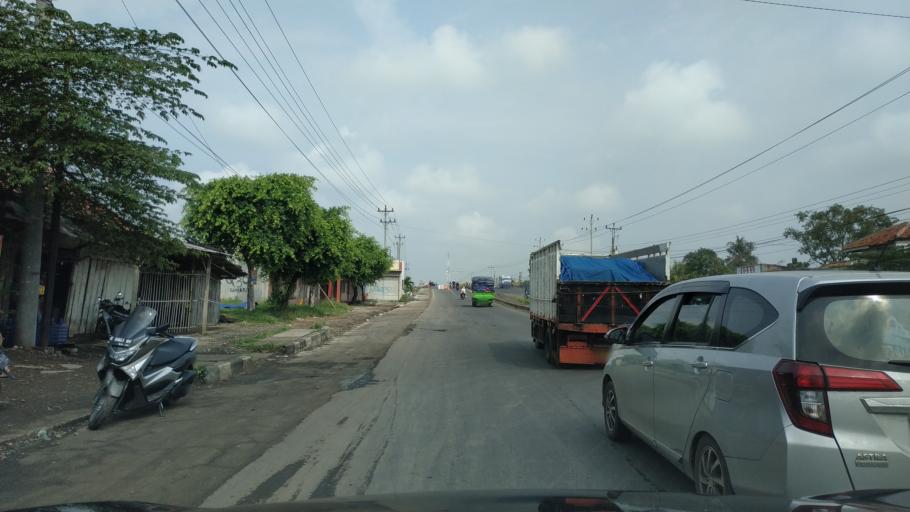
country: ID
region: Central Java
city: Bulakamba
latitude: -6.8714
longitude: 108.8935
